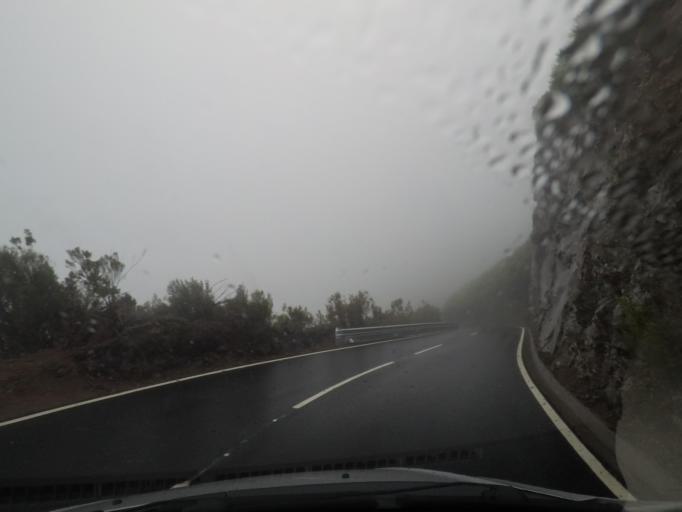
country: PT
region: Madeira
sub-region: Santana
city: Santana
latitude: 32.7708
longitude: -16.9173
